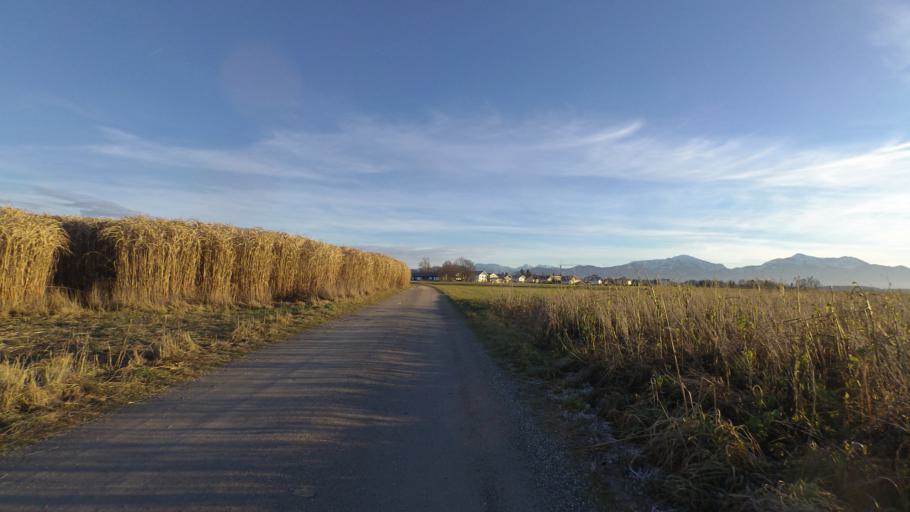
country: DE
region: Bavaria
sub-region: Upper Bavaria
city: Chieming
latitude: 47.9015
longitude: 12.5328
